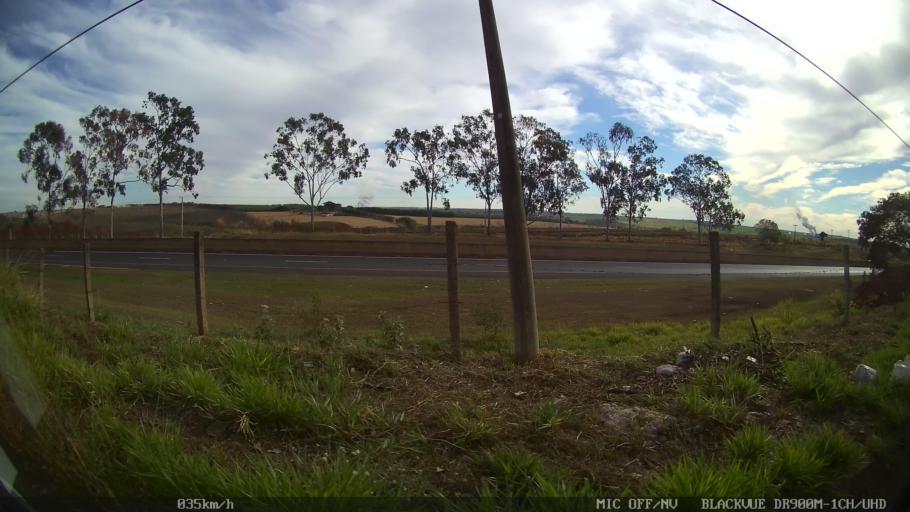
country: BR
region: Sao Paulo
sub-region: Catanduva
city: Catanduva
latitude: -21.1255
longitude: -49.0003
